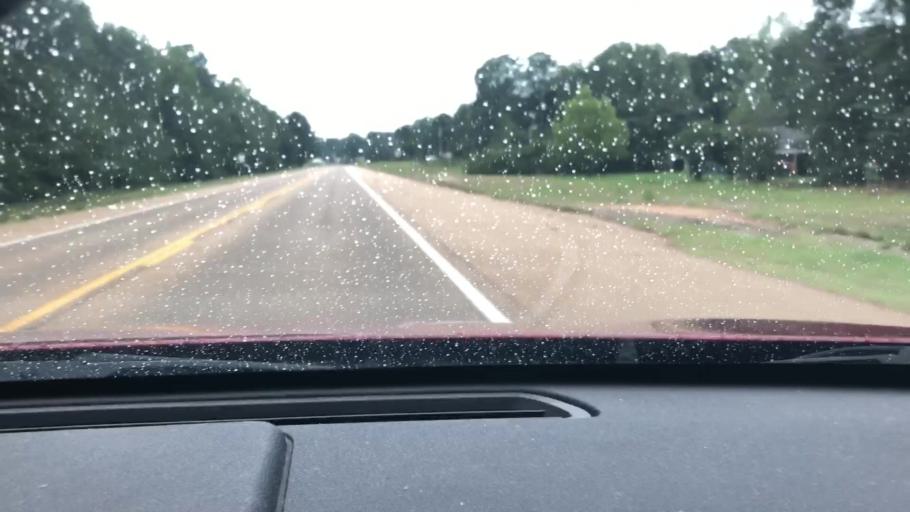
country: US
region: Arkansas
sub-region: Lafayette County
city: Stamps
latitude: 33.3590
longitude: -93.4231
